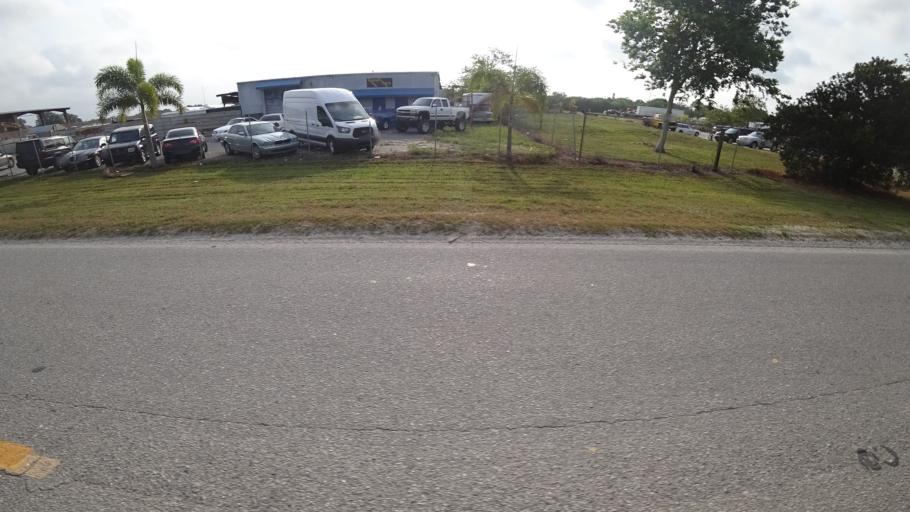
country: US
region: Florida
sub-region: Manatee County
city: Whitfield
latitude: 27.4267
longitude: -82.5219
